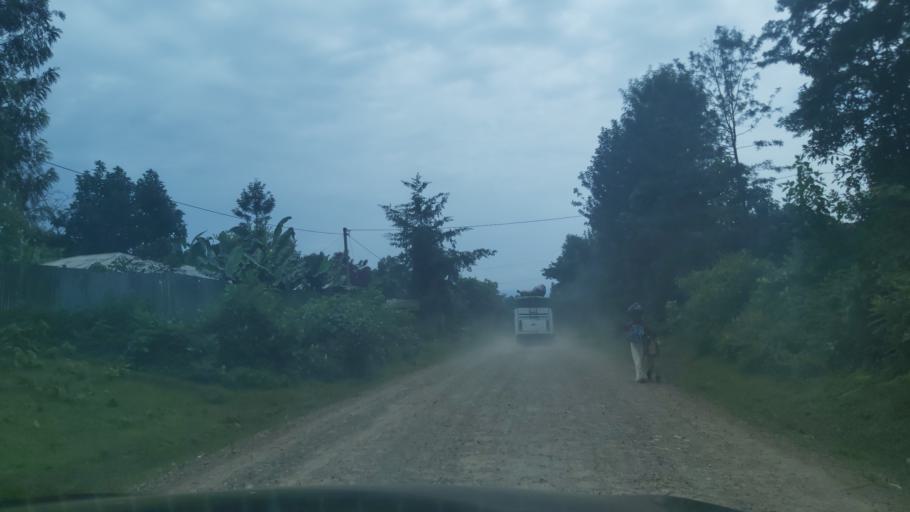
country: ET
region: Oromiya
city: Jima
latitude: 7.7349
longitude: 36.7694
